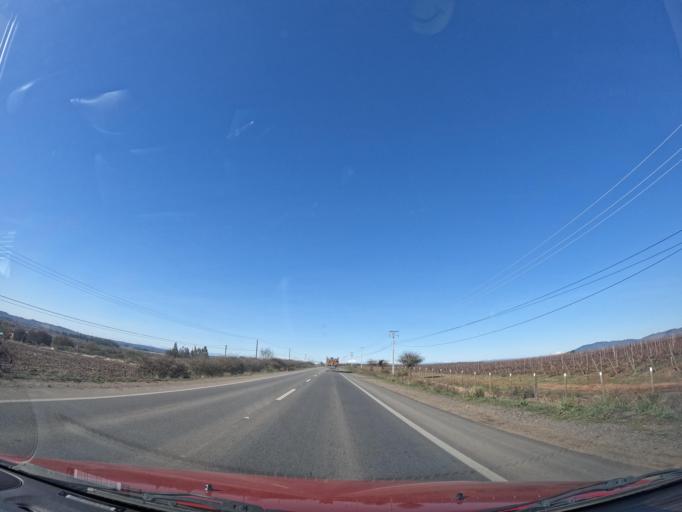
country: CL
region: Maule
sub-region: Provincia de Cauquenes
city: Cauquenes
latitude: -35.9637
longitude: -72.2382
